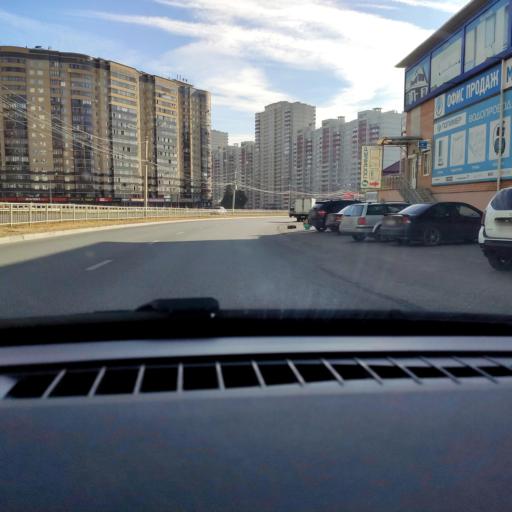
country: RU
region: Voronezj
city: Voronezh
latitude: 51.7134
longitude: 39.1921
